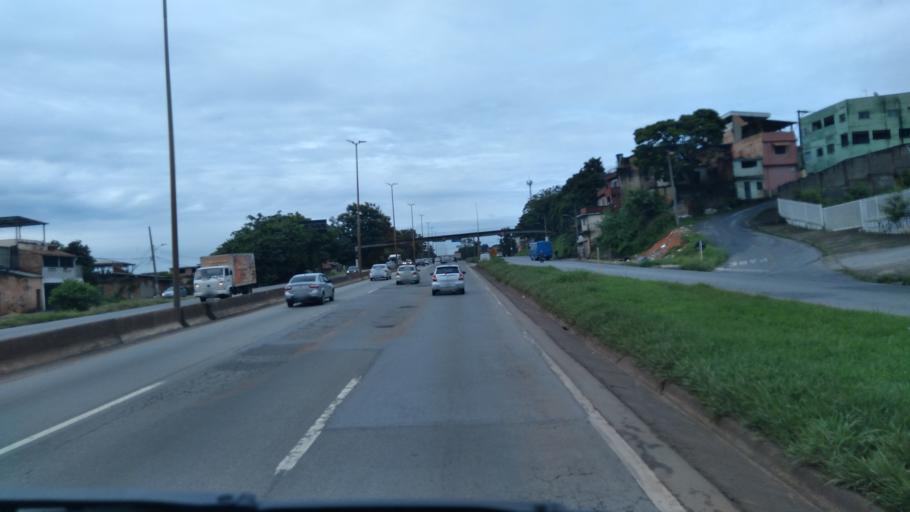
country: BR
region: Minas Gerais
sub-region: Contagem
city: Contagem
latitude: -19.9197
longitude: -43.9994
